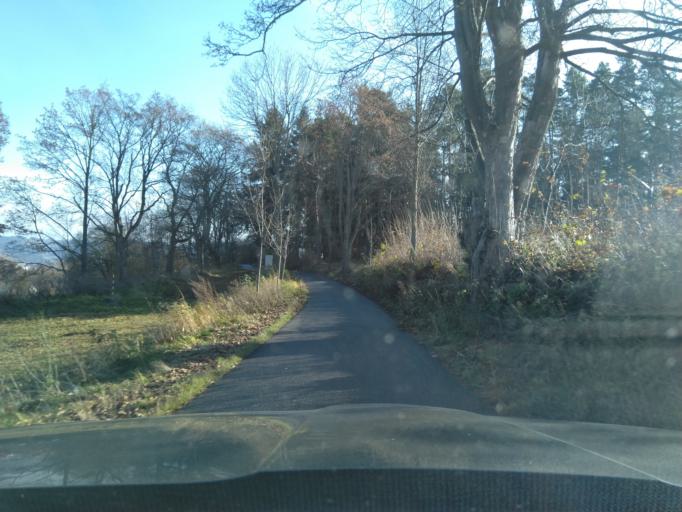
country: CZ
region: Jihocesky
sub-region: Okres Prachatice
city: Vimperk
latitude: 49.0588
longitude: 13.7653
